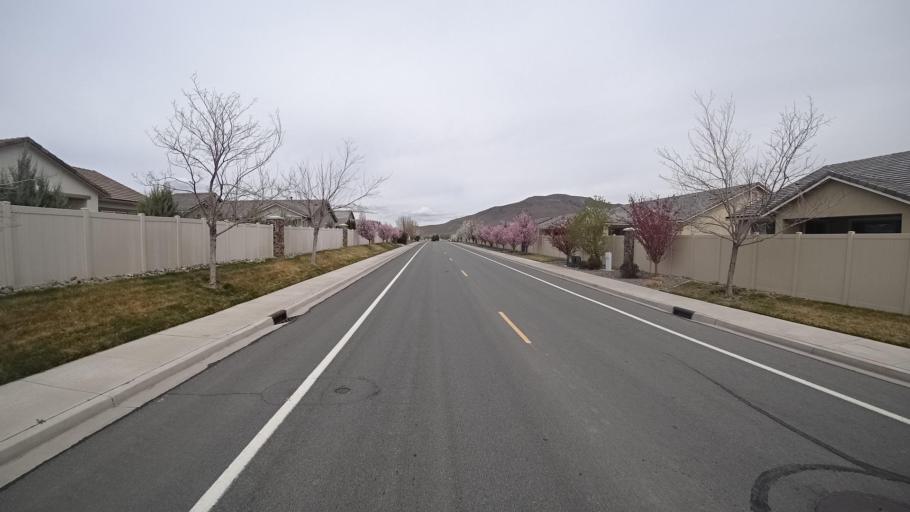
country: US
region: Nevada
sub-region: Washoe County
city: Sparks
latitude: 39.4345
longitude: -119.7210
